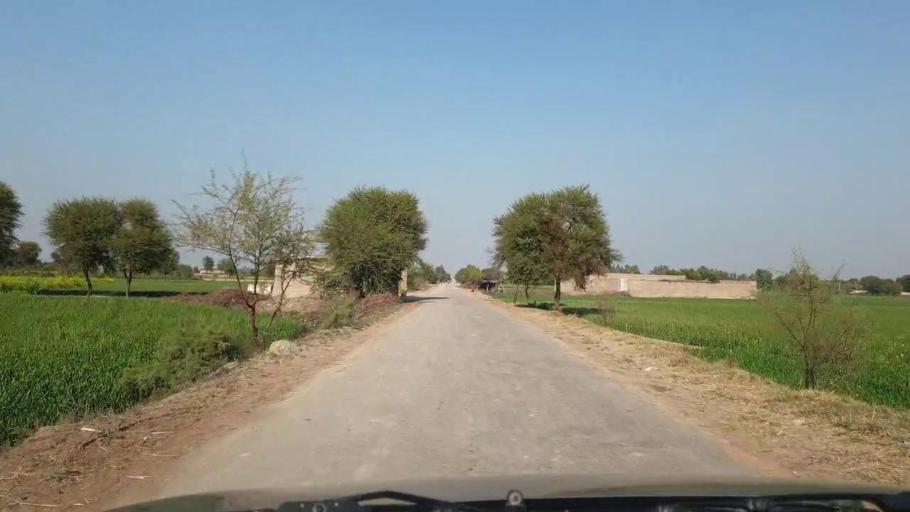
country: PK
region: Sindh
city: Jhol
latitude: 25.9398
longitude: 68.8813
